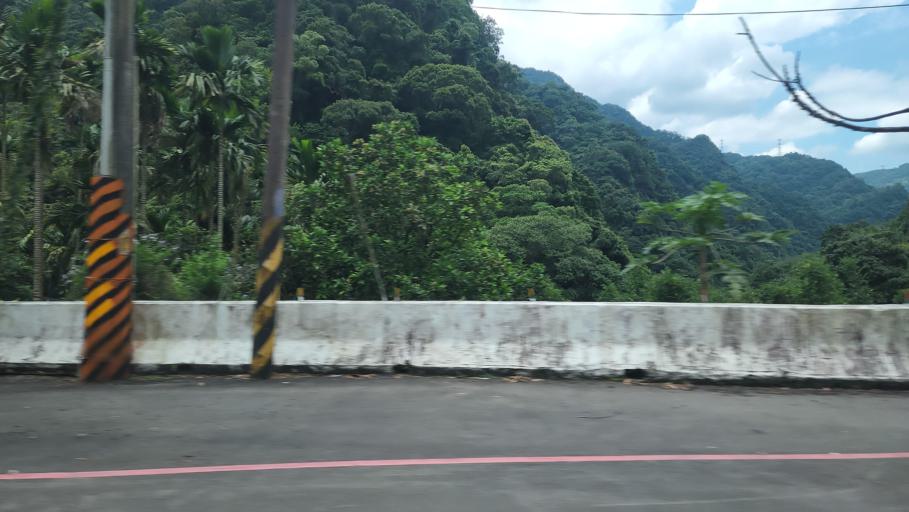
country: TW
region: Taiwan
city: Daxi
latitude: 24.8633
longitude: 121.4321
